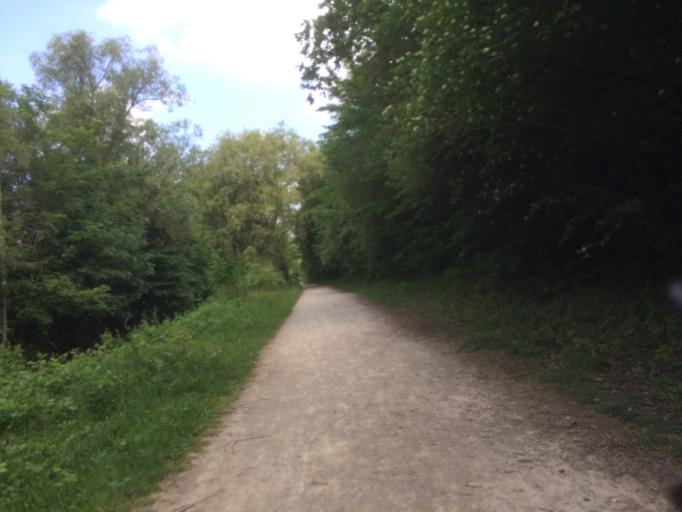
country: FR
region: Ile-de-France
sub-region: Departement de l'Essonne
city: Ris-Orangis
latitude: 48.6404
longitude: 2.4172
